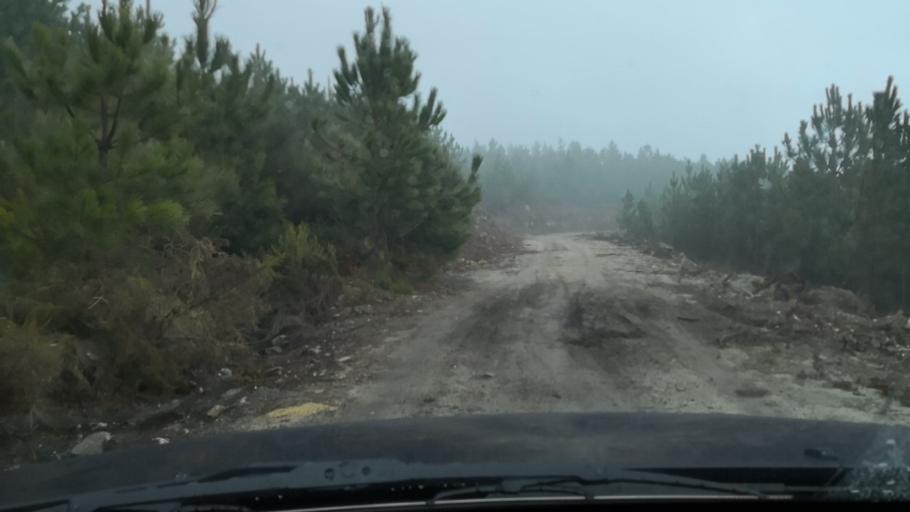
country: PT
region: Vila Real
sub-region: Vila Real
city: Vila Real
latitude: 41.3696
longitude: -7.7467
